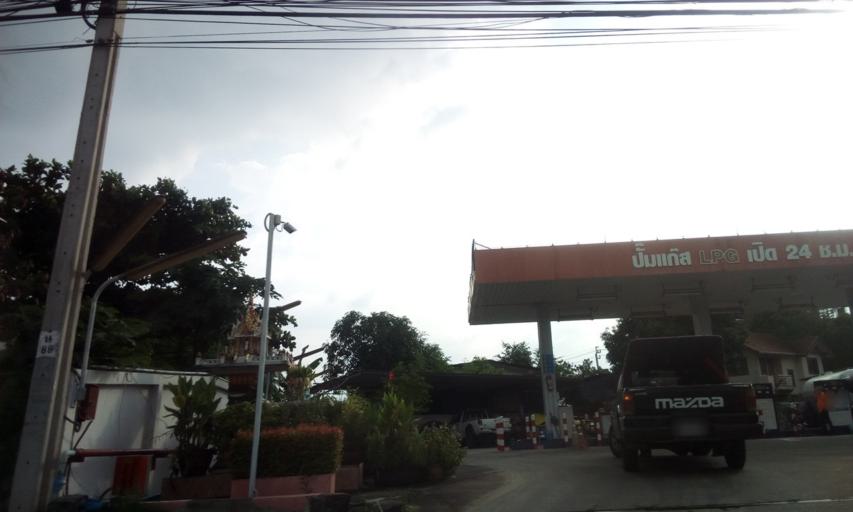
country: TH
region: Nonthaburi
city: Pak Kret
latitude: 13.9390
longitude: 100.5434
